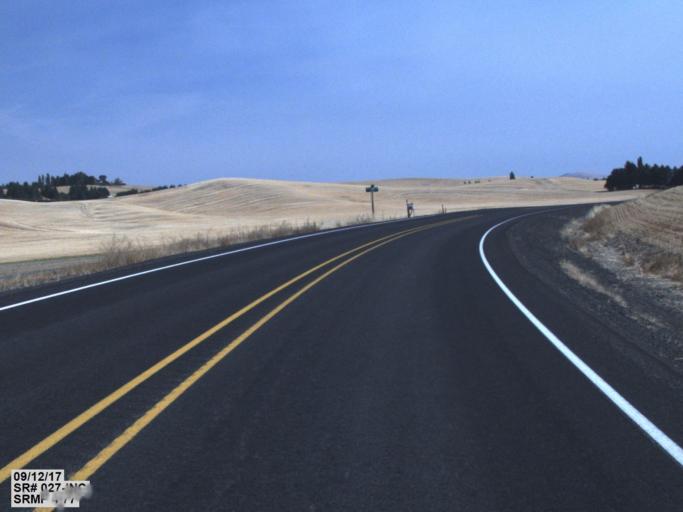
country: US
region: Washington
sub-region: Whitman County
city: Pullman
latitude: 46.7927
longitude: -117.1461
